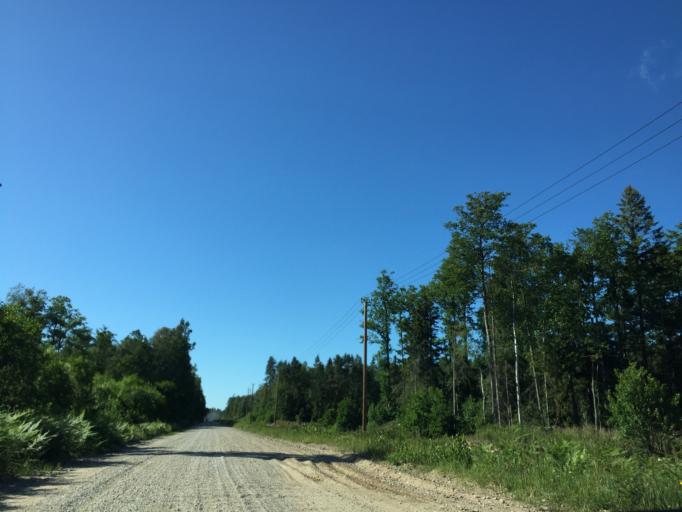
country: LV
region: Ventspils
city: Ventspils
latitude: 57.5547
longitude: 21.7374
